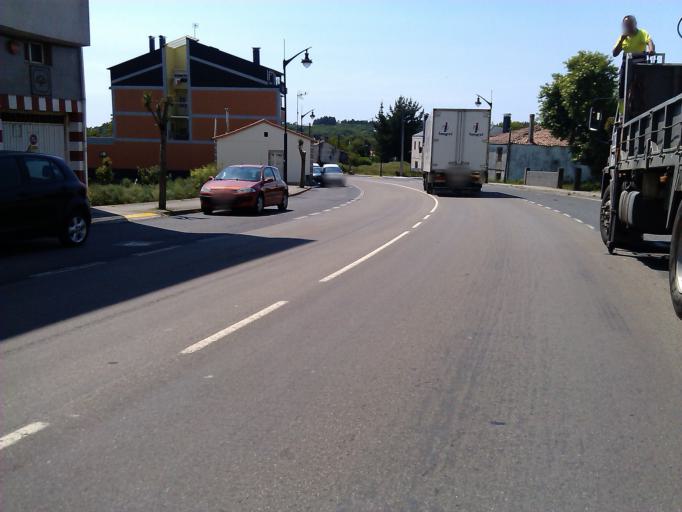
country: ES
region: Galicia
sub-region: Provincia de Lugo
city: Monterroso
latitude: 42.8739
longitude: -7.8711
